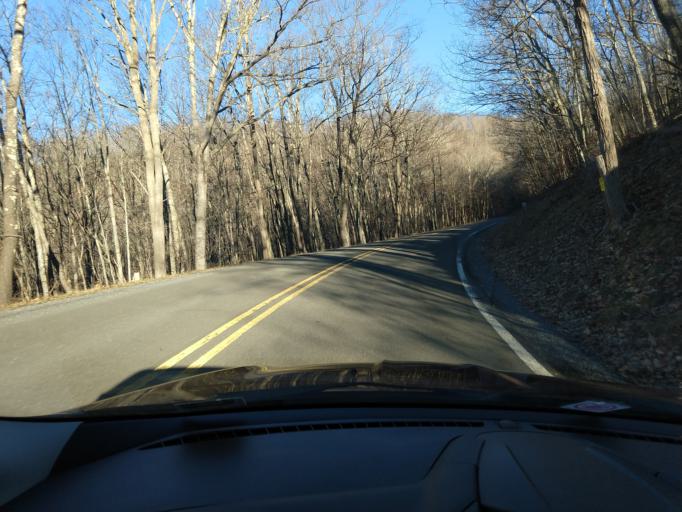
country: US
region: Virginia
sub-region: Highland County
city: Monterey
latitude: 38.4605
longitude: -79.6650
